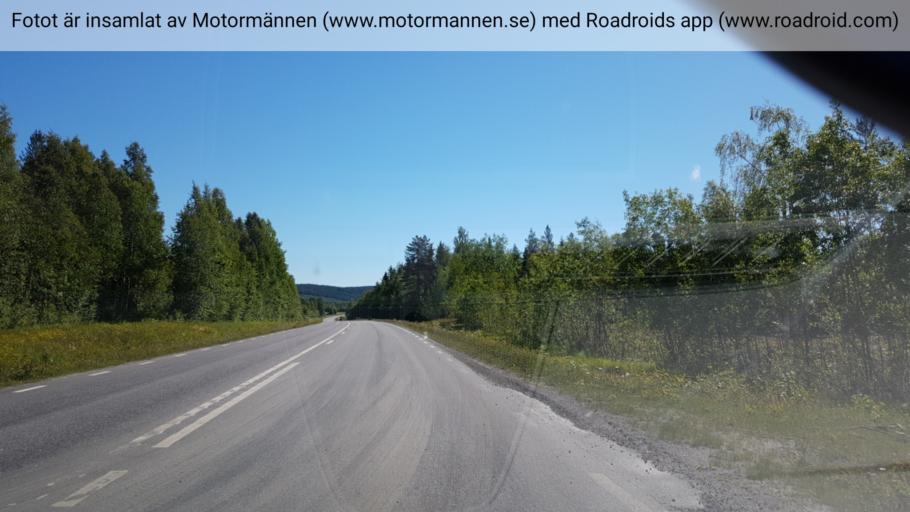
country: SE
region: Norrbotten
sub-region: Bodens Kommun
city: Boden
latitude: 65.8497
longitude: 21.5414
